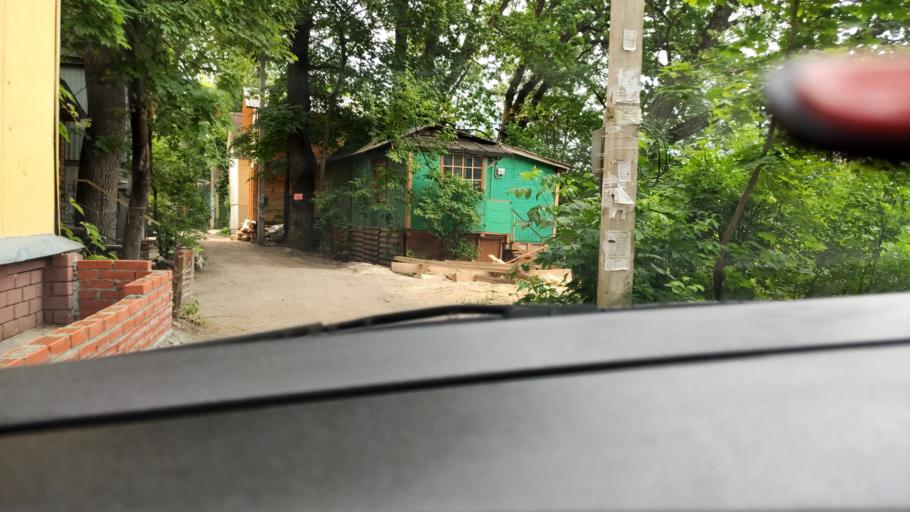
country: RU
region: Voronezj
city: Ramon'
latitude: 51.8877
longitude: 39.3468
